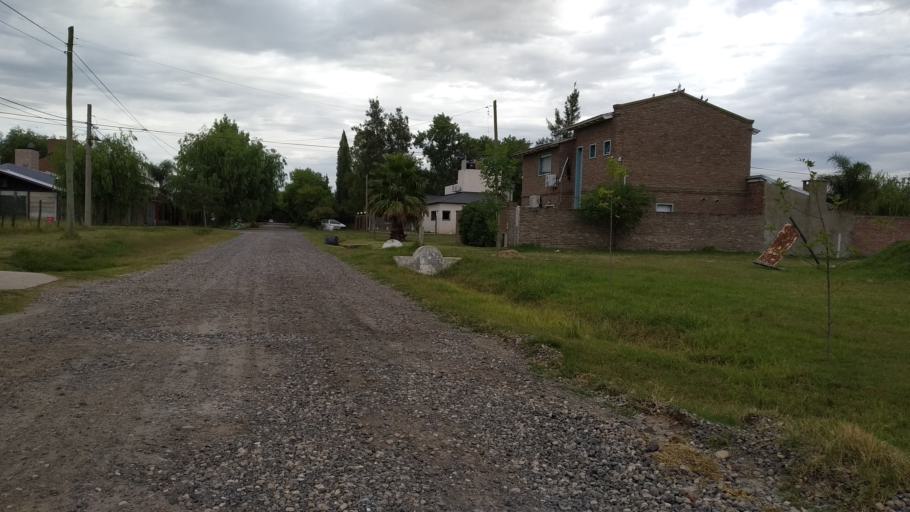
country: AR
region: Santa Fe
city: Funes
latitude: -32.9306
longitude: -60.8015
